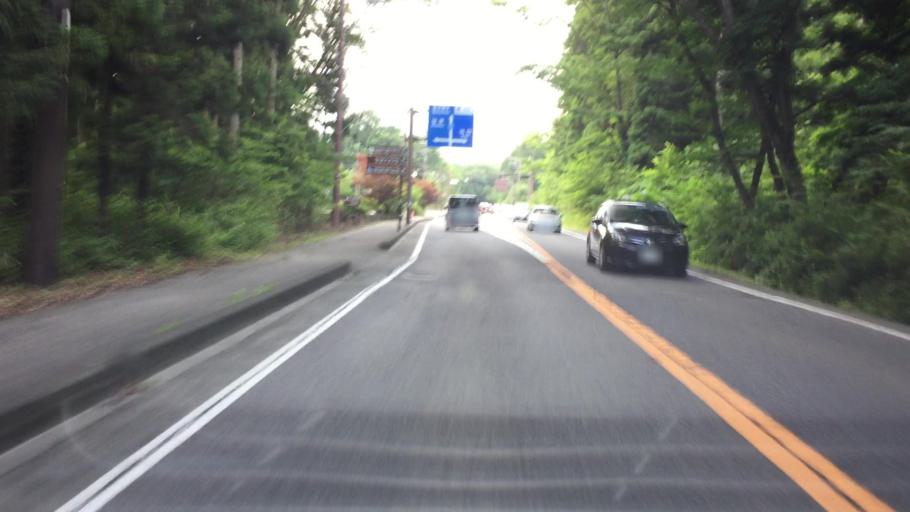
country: JP
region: Tochigi
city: Kuroiso
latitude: 37.0247
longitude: 140.0253
